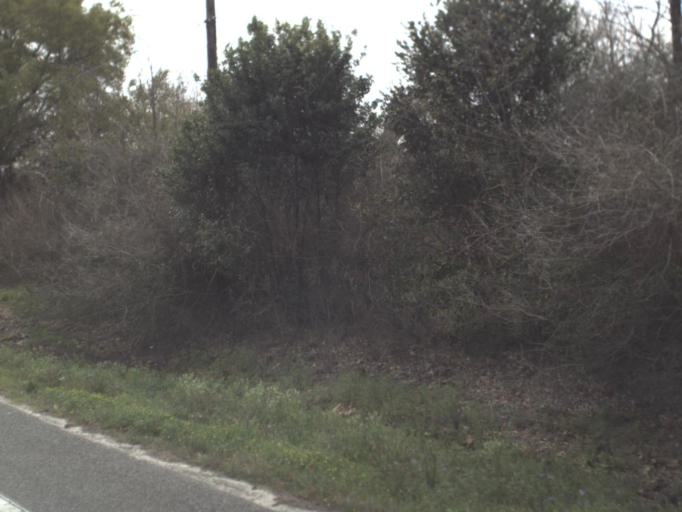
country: US
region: Florida
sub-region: Gulf County
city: Wewahitchka
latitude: 30.0400
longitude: -85.1843
